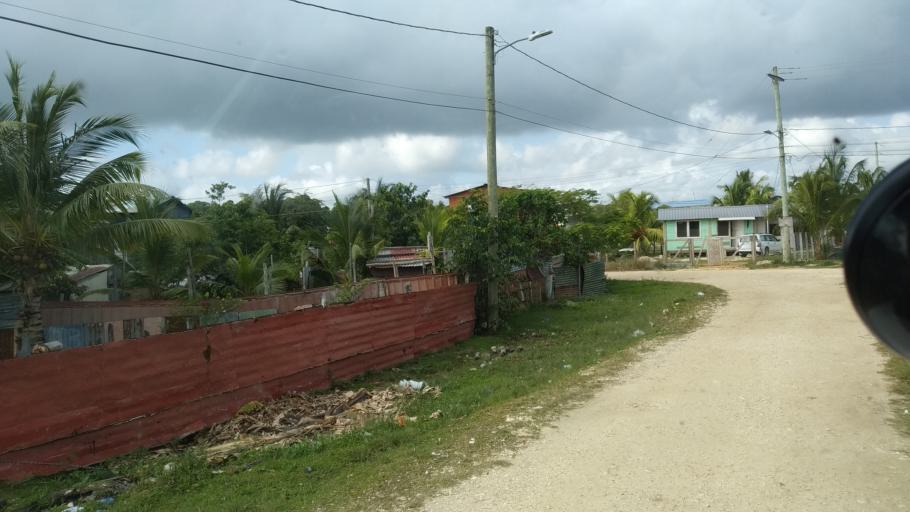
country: BZ
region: Belize
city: Belize City
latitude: 17.5153
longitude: -88.2335
